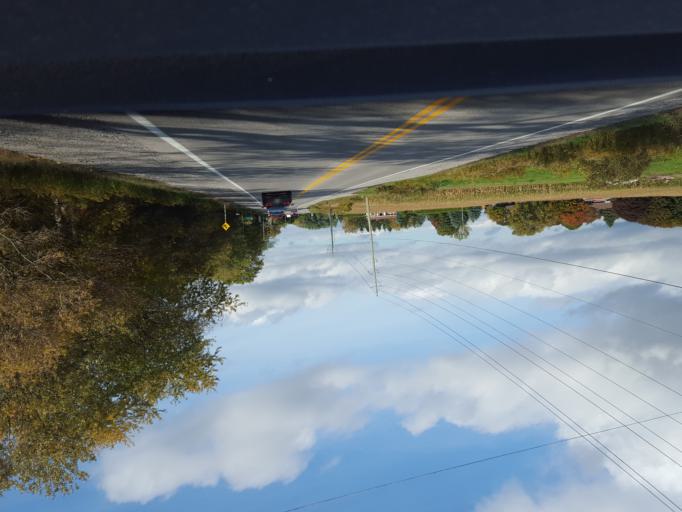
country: CA
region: Ontario
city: Oshawa
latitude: 43.9822
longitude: -78.6623
